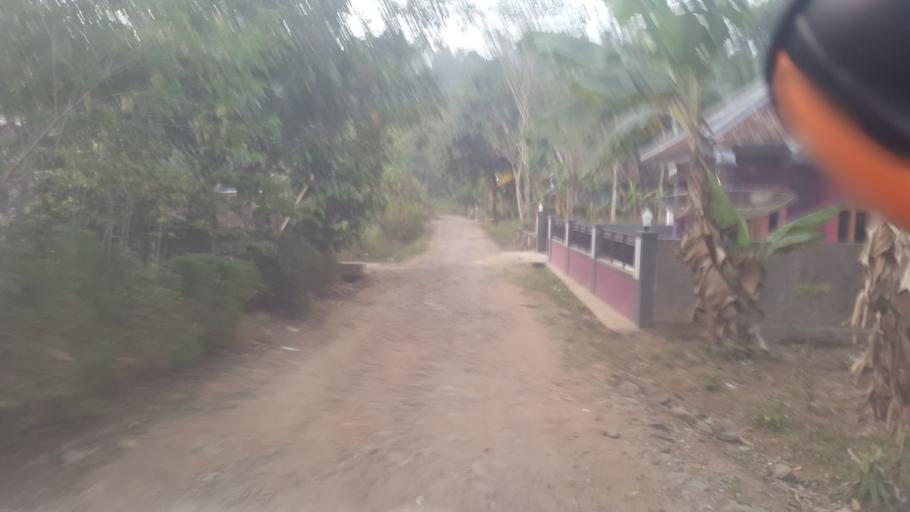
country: ID
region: West Java
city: Sukamaju
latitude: -7.0020
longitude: 106.8829
